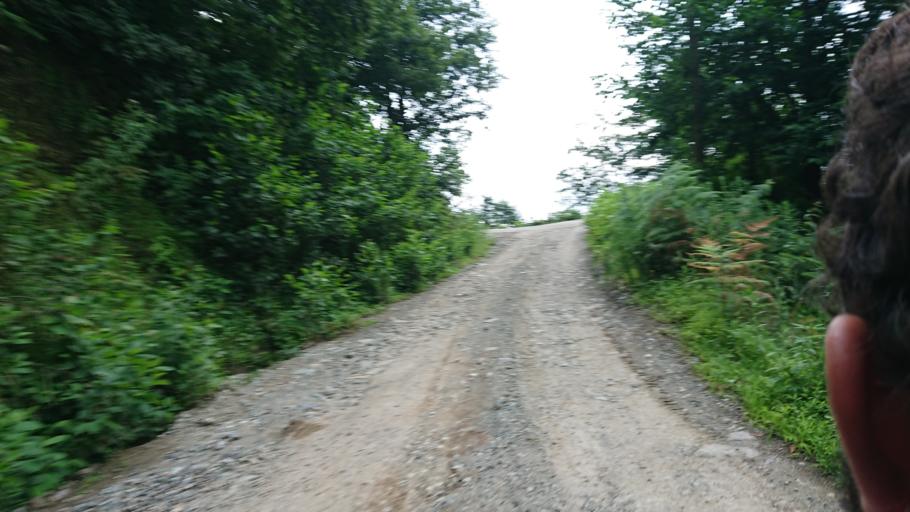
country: TR
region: Rize
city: Rize
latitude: 40.9889
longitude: 40.5156
